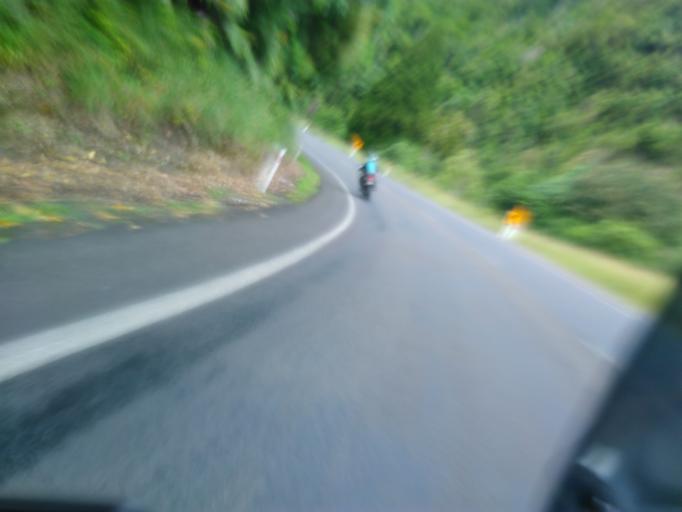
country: NZ
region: Bay of Plenty
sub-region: Opotiki District
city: Opotiki
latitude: -38.3014
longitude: 177.3929
